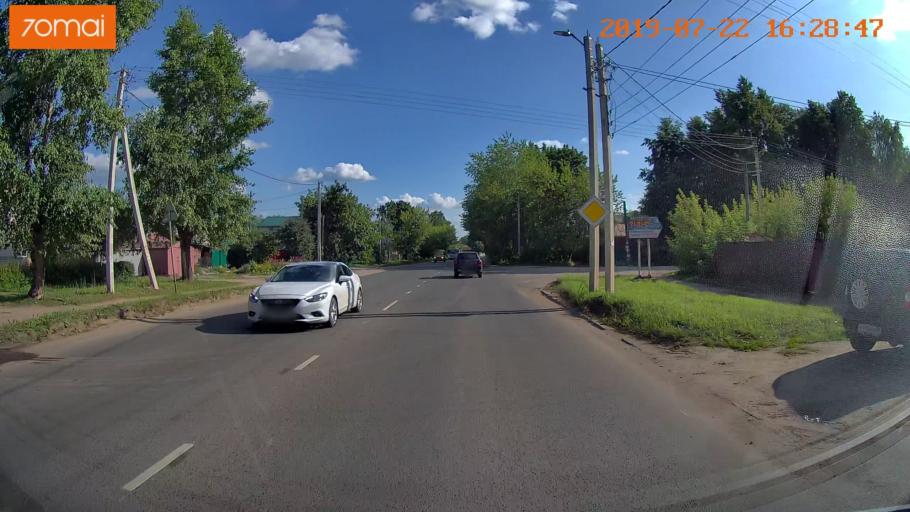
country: RU
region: Ivanovo
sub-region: Gorod Ivanovo
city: Ivanovo
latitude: 57.0366
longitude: 40.9505
